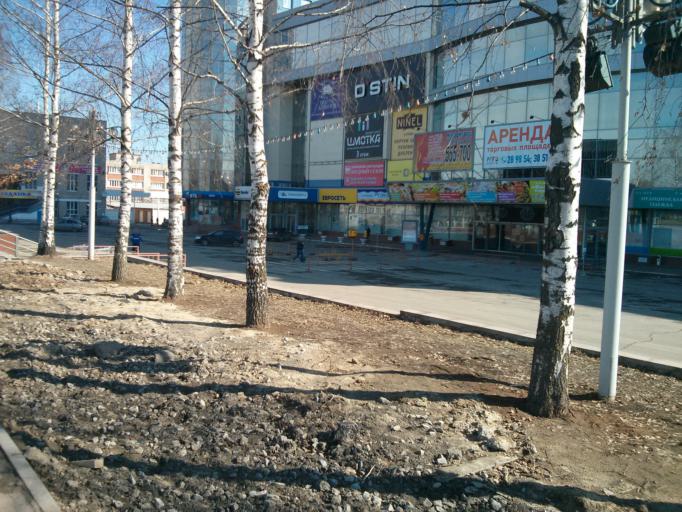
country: RU
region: Chuvashia
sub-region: Cheboksarskiy Rayon
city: Cheboksary
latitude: 56.1016
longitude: 47.2639
